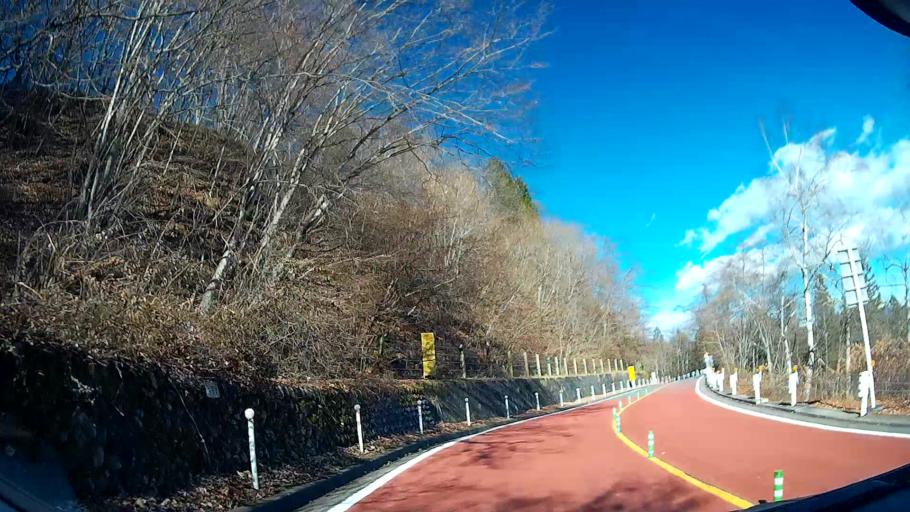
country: JP
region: Yamanashi
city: Uenohara
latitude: 35.7472
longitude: 139.0416
